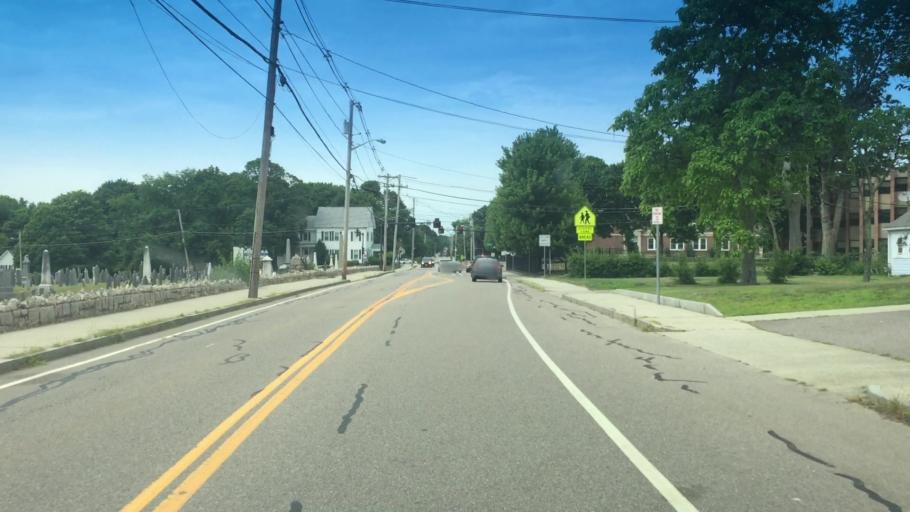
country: US
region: Massachusetts
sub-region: Norfolk County
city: Franklin
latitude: 42.0823
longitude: -71.4032
